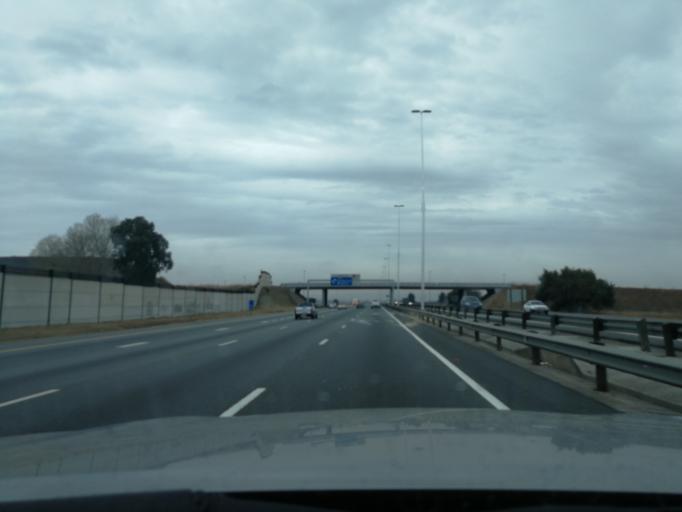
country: ZA
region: Gauteng
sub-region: Ekurhuleni Metropolitan Municipality
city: Germiston
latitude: -26.2836
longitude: 28.1516
